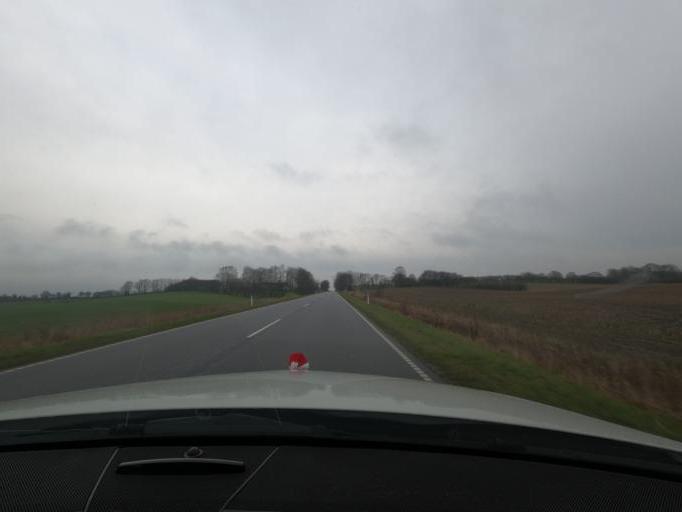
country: DK
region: South Denmark
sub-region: Haderslev Kommune
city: Vojens
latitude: 55.1759
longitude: 9.3911
